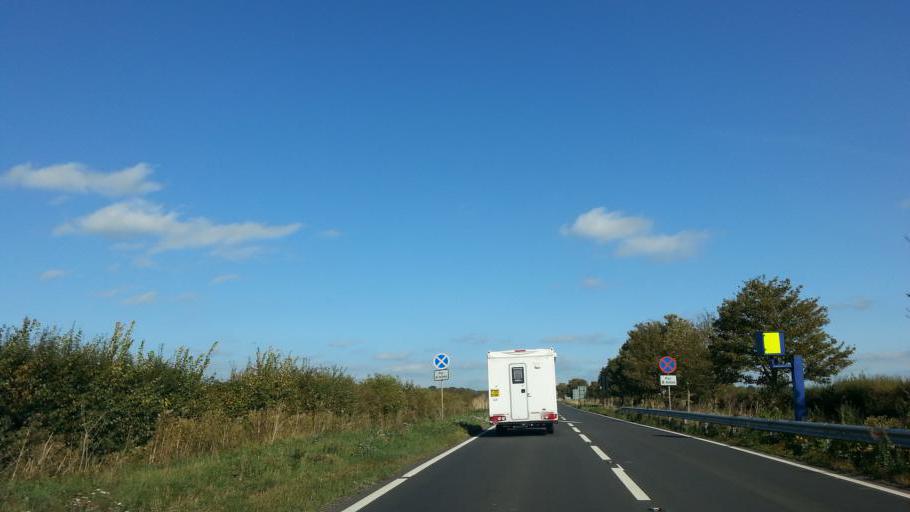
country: GB
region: England
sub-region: Northamptonshire
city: Thrapston
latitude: 52.4231
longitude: -0.4932
